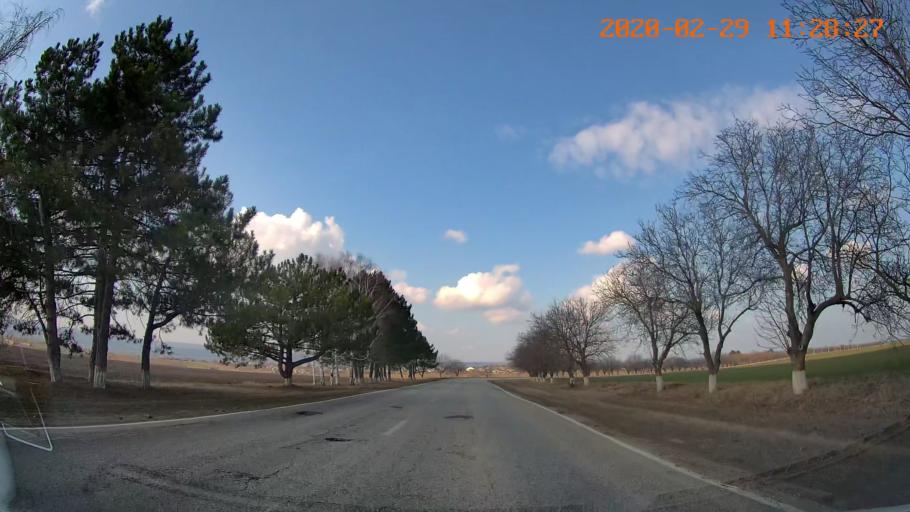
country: MD
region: Telenesti
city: Cocieri
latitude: 47.4814
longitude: 29.1351
